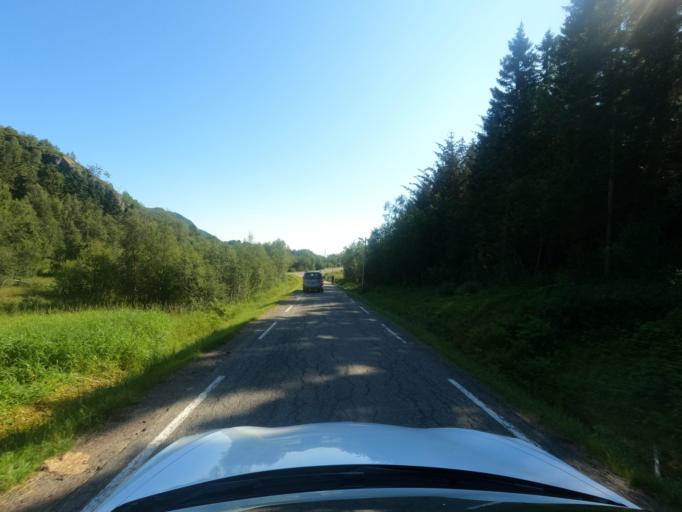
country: NO
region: Nordland
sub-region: Hadsel
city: Stokmarknes
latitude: 68.3030
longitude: 15.0381
